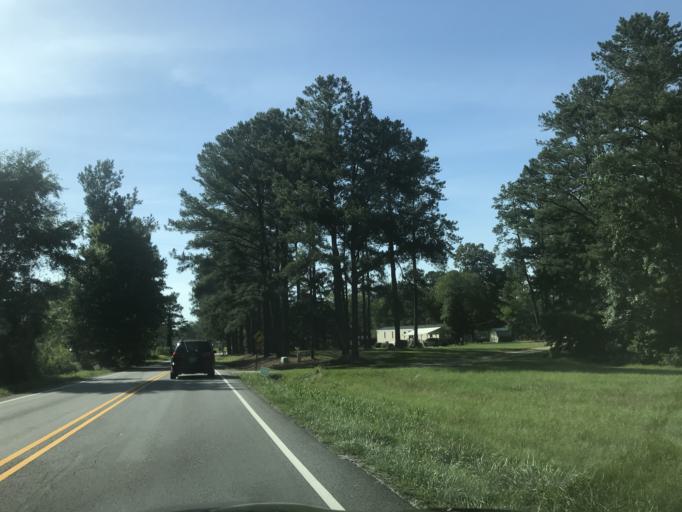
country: US
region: North Carolina
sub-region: Wake County
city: Garner
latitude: 35.6679
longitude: -78.5727
